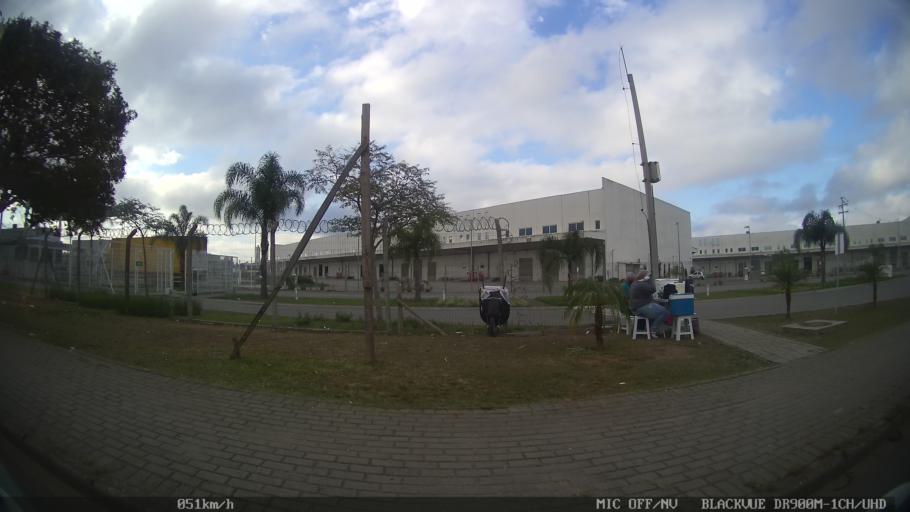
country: BR
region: Parana
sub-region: Pinhais
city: Pinhais
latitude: -25.4329
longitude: -49.1650
